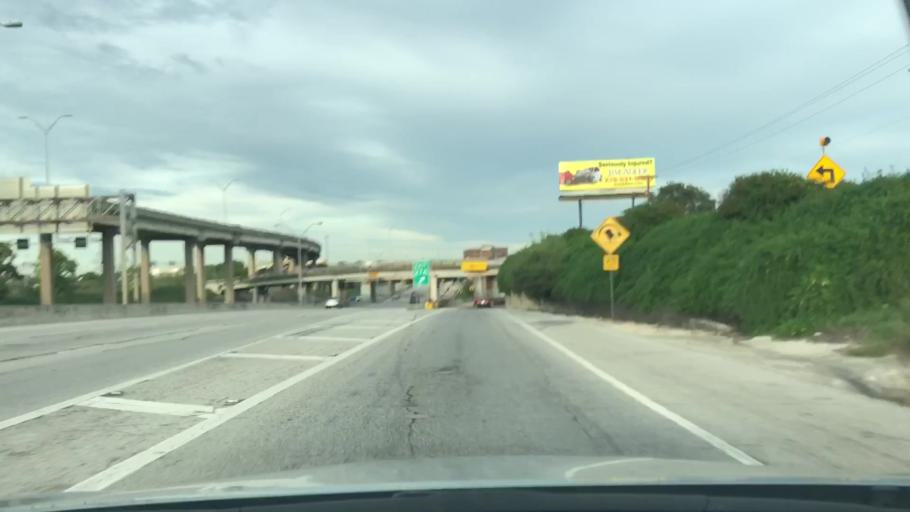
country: US
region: Texas
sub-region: Bexar County
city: Windcrest
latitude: 29.5197
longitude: -98.3978
